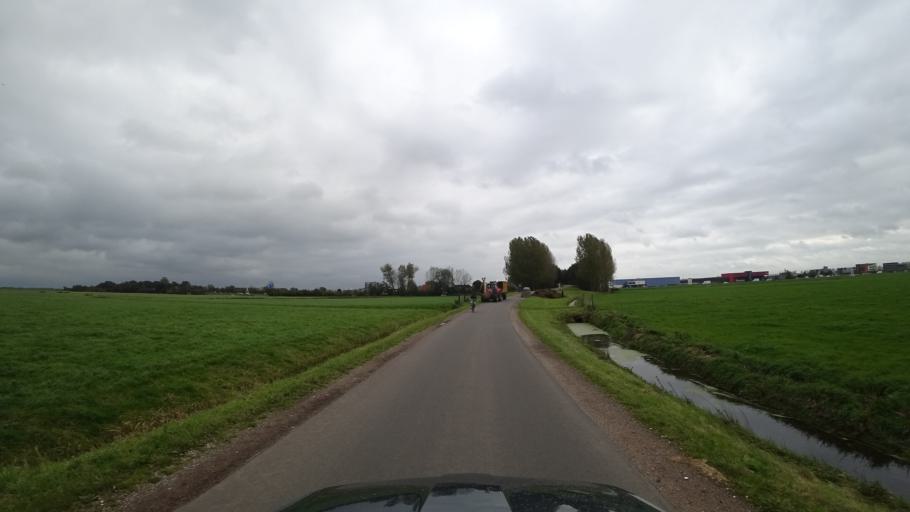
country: NL
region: Gelderland
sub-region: Gemeente Nijkerk
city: Nijkerk
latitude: 52.2375
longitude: 5.4587
